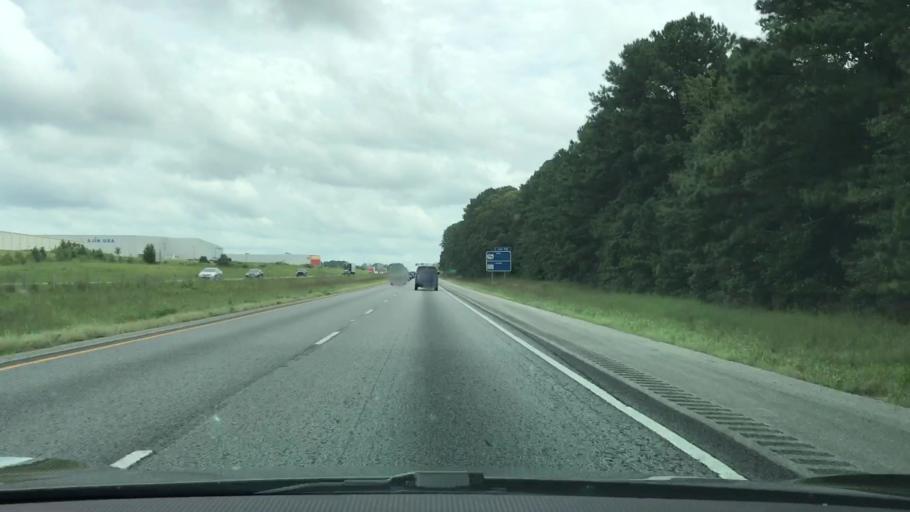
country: US
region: Alabama
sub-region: Chambers County
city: Huguley
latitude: 32.7364
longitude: -85.2887
